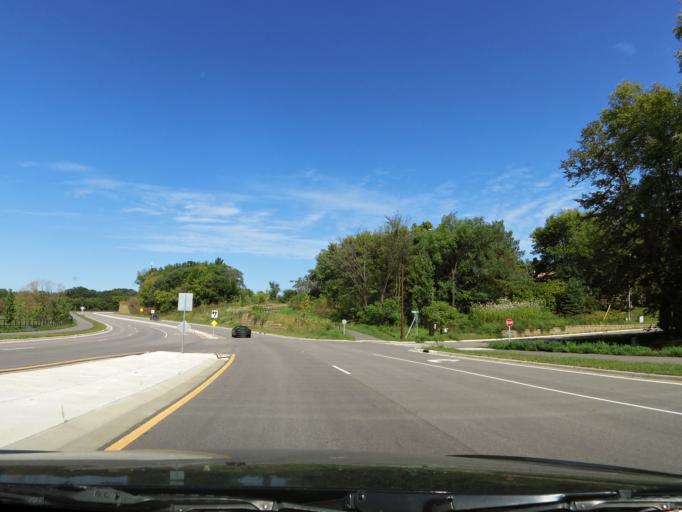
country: US
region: Minnesota
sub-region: Carver County
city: Chanhassen
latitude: 44.8323
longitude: -93.5353
